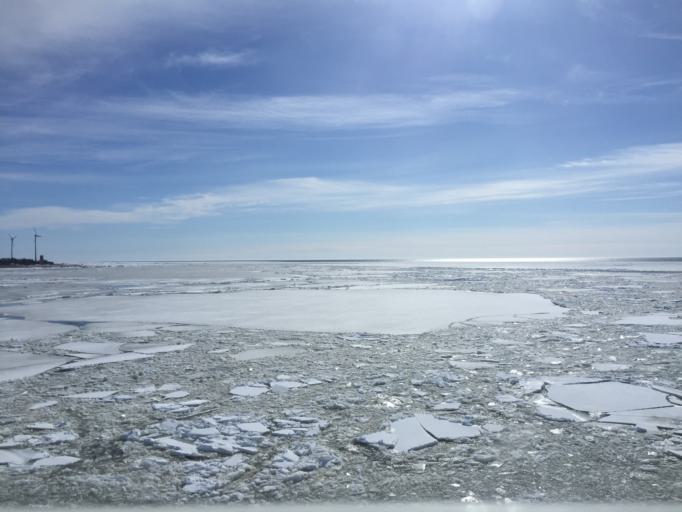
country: EE
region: Laeaene
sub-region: Lihula vald
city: Lihula
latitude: 58.5765
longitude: 23.4927
